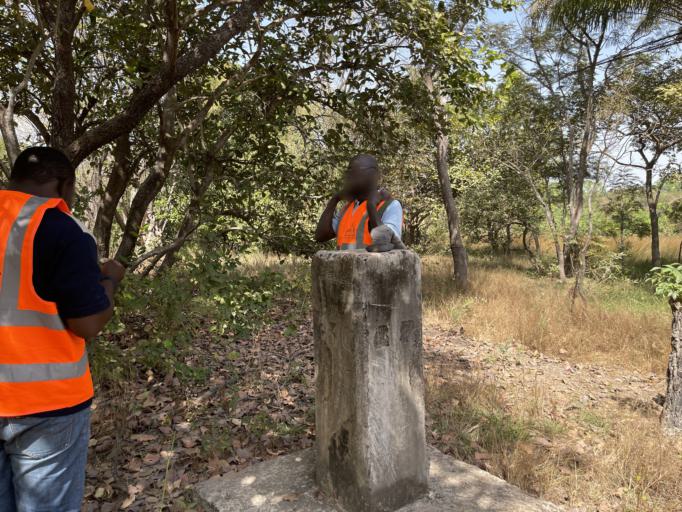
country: SN
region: Sedhiou
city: Sedhiou
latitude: 12.4329
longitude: -15.7373
